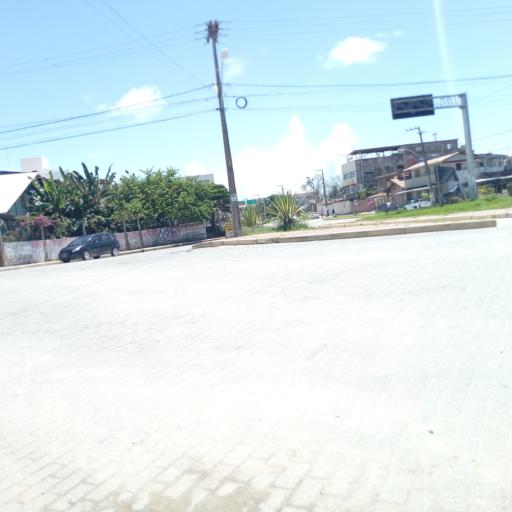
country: BR
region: Pernambuco
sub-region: Ipojuca
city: Ipojuca
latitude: -8.5072
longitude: -35.0083
